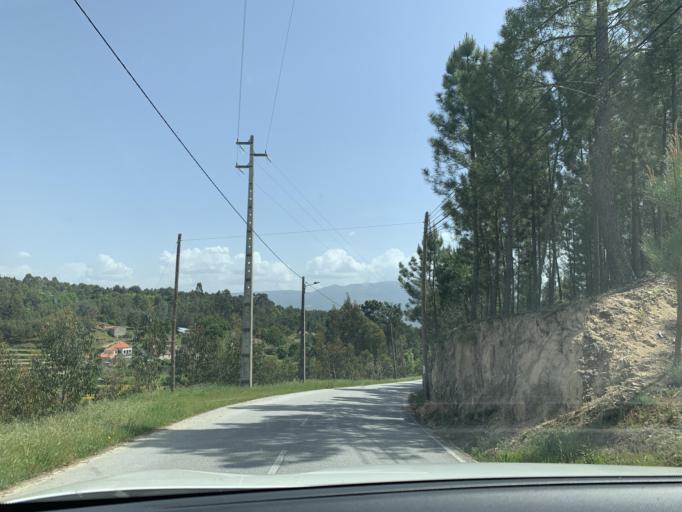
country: PT
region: Guarda
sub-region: Fornos de Algodres
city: Fornos de Algodres
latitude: 40.5952
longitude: -7.6307
